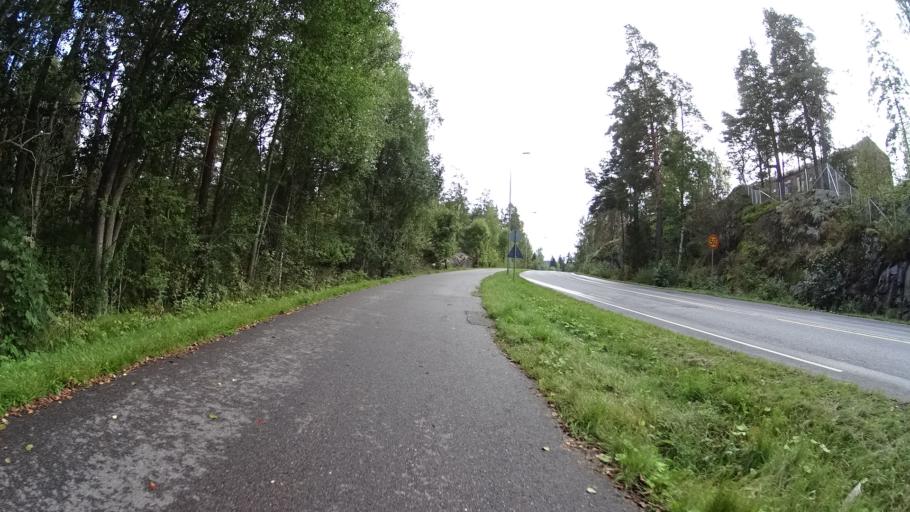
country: FI
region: Uusimaa
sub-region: Helsinki
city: Espoo
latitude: 60.2272
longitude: 24.6682
